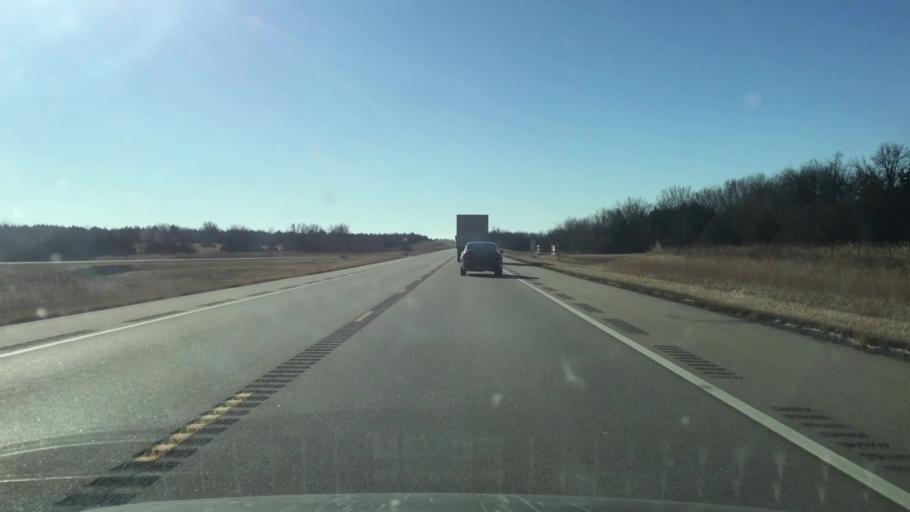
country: US
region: Kansas
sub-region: Allen County
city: Iola
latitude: 38.0396
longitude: -95.3806
